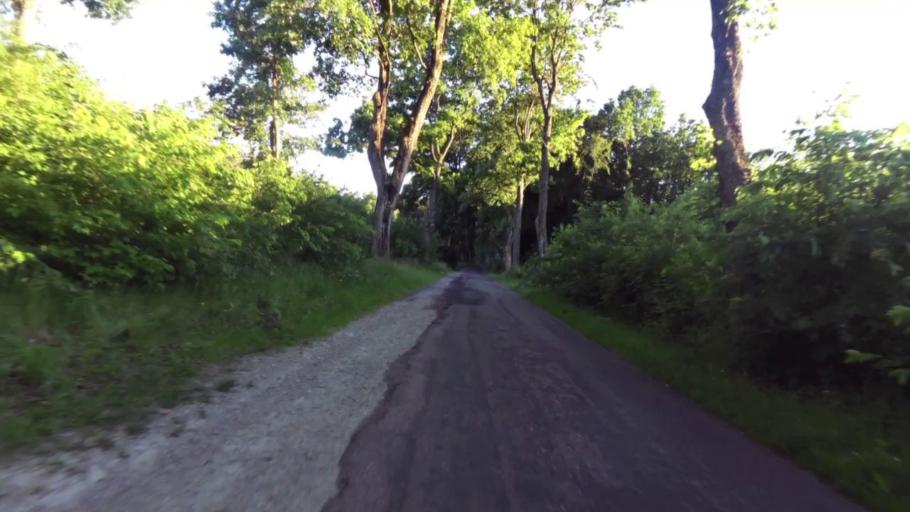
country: PL
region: West Pomeranian Voivodeship
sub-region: Koszalin
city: Koszalin
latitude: 54.0650
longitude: 16.1234
